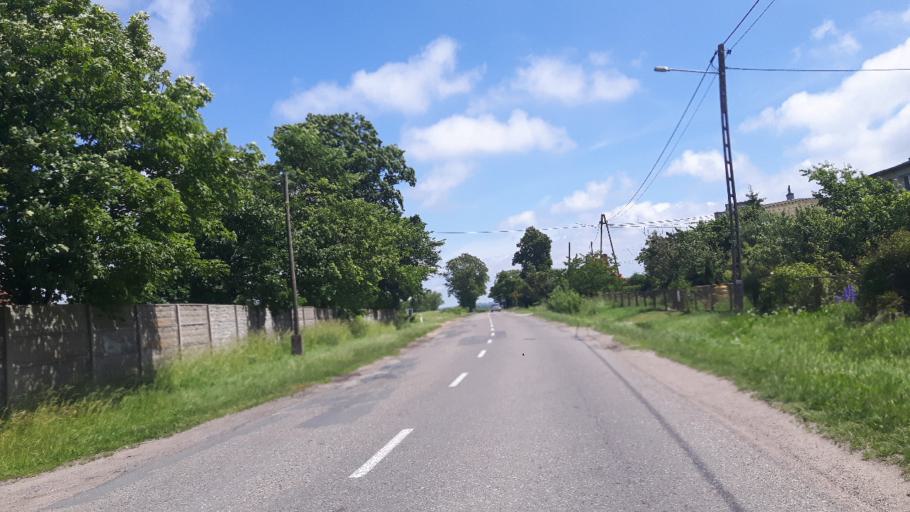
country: PL
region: Pomeranian Voivodeship
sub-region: Powiat slupski
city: Ustka
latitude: 54.5204
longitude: 16.7696
